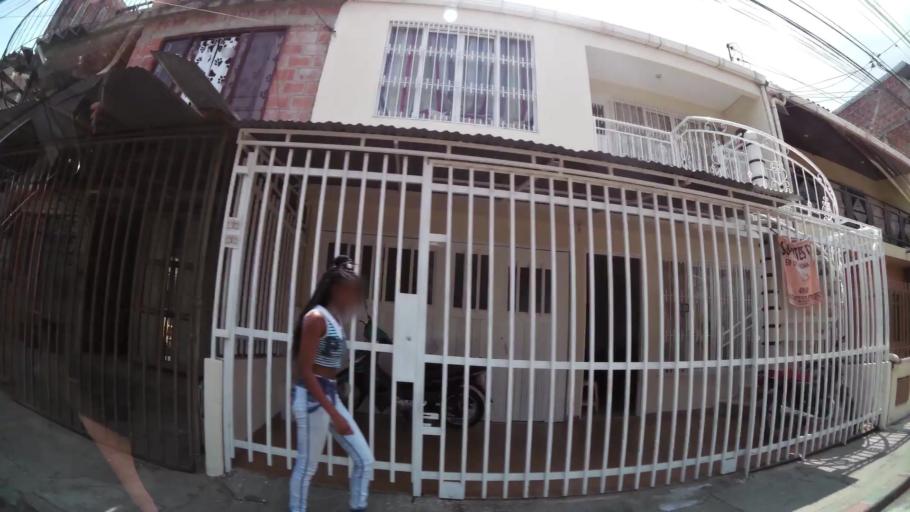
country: CO
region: Valle del Cauca
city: Cali
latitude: 3.4731
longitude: -76.4833
